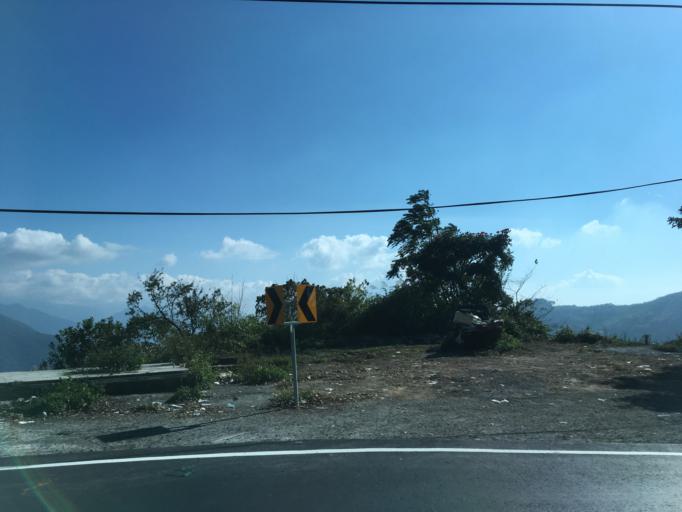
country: TW
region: Taiwan
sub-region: Chiayi
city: Jiayi Shi
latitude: 23.4050
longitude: 120.6548
